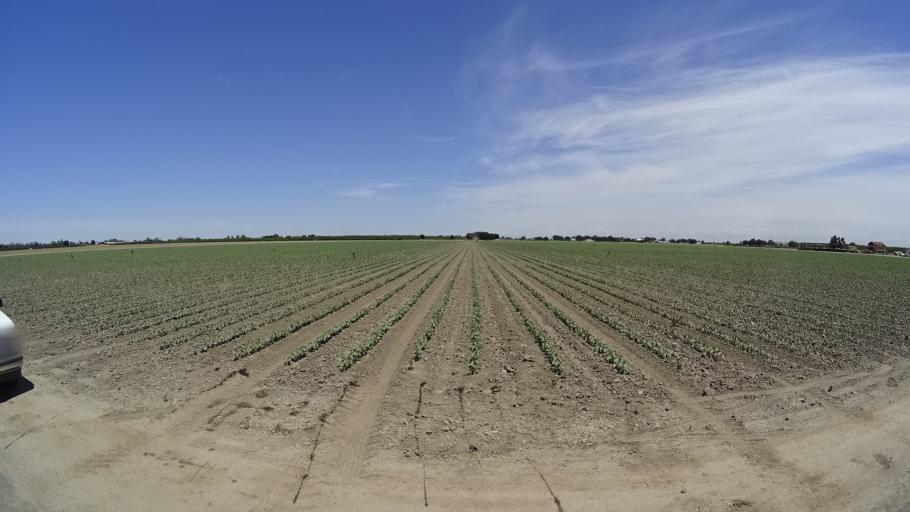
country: US
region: California
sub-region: Kings County
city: Lemoore
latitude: 36.3498
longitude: -119.7882
